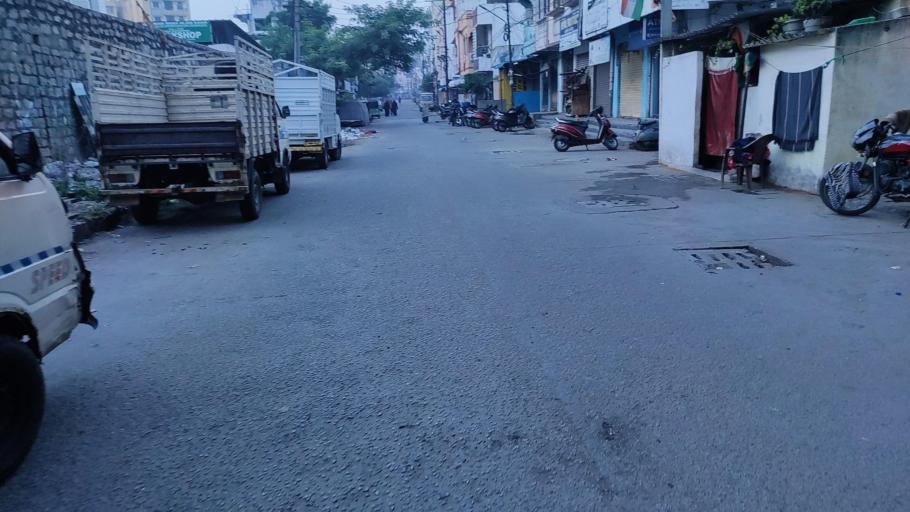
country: IN
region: Telangana
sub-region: Rangareddi
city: Gaddi Annaram
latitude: 17.3718
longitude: 78.4925
